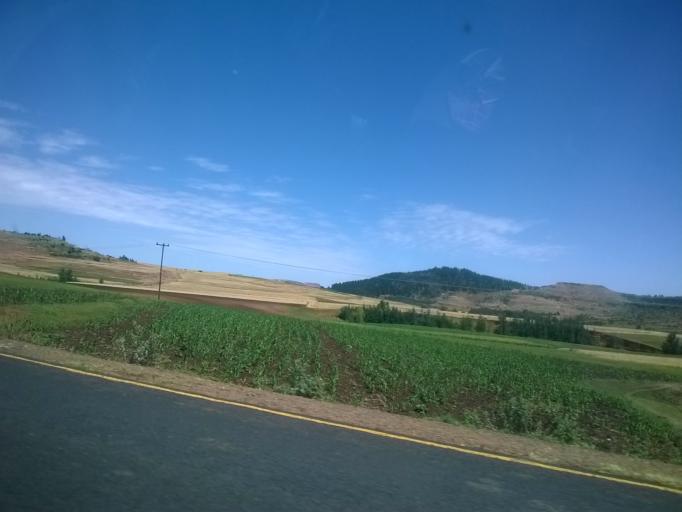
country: LS
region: Leribe
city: Maputsoe
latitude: -29.0873
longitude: 27.9478
